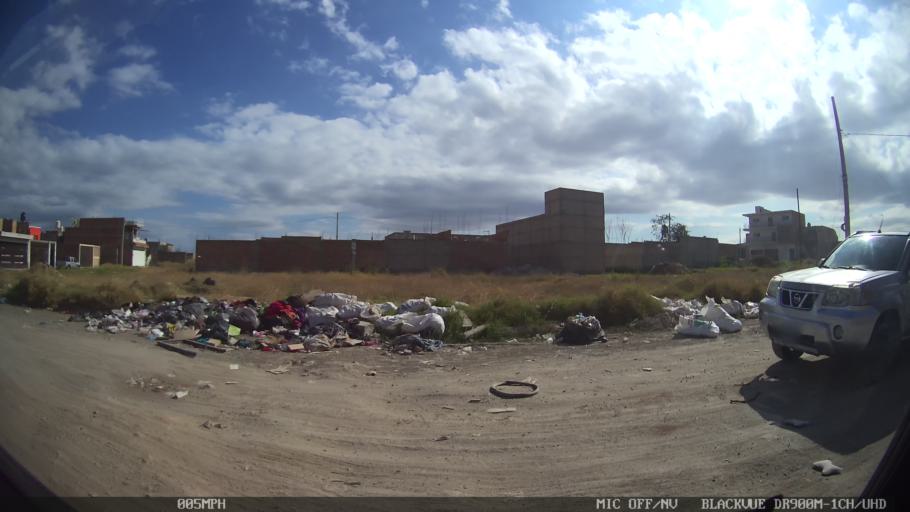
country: MX
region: Jalisco
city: Tonala
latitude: 20.6542
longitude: -103.2423
